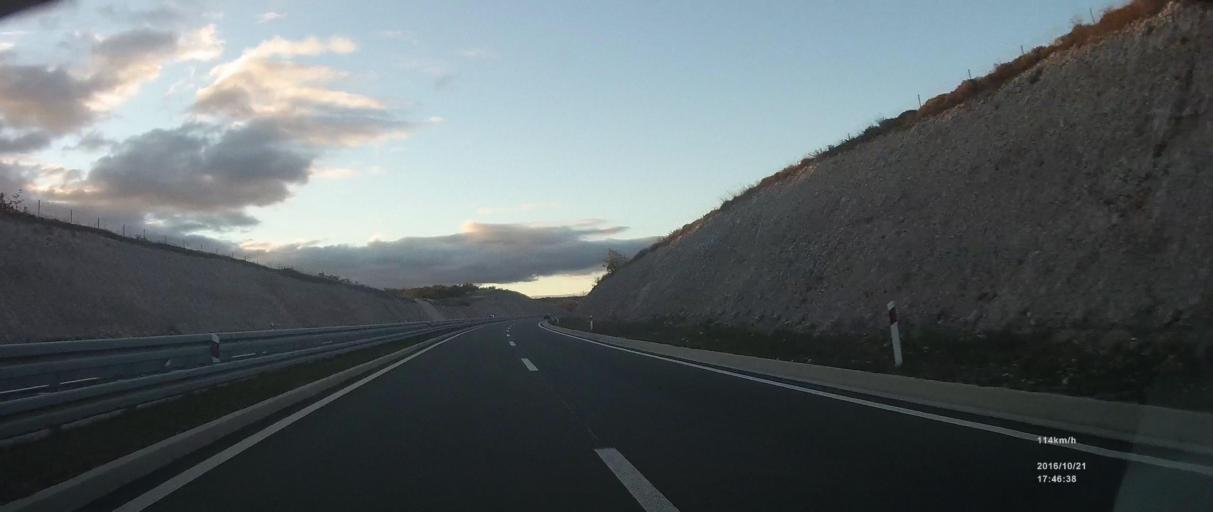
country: HR
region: Primorsko-Goranska
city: Krasica
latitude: 45.3033
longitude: 14.5576
